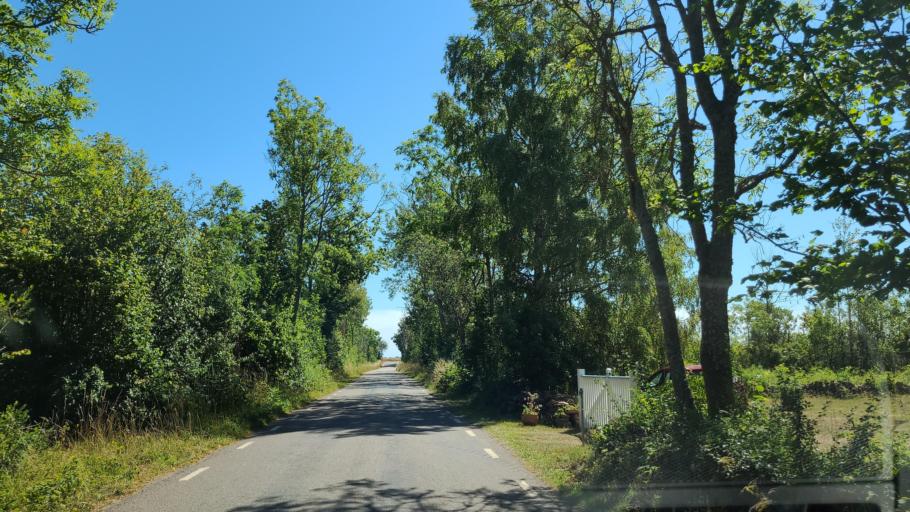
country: SE
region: Kalmar
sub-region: Borgholms Kommun
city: Borgholm
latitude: 56.7440
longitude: 16.7010
